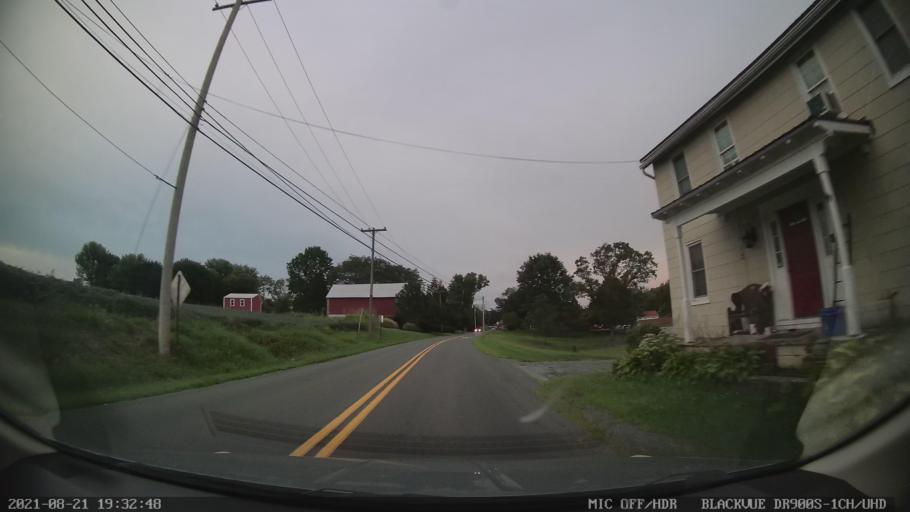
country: US
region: Pennsylvania
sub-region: Berks County
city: Oley
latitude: 40.3967
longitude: -75.7990
